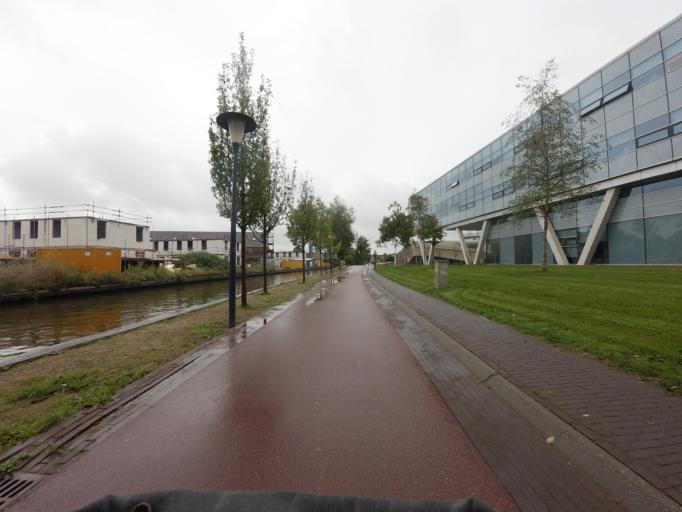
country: NL
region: Friesland
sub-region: Gemeente Leeuwarden
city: Bilgaard
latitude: 53.2118
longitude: 5.8014
